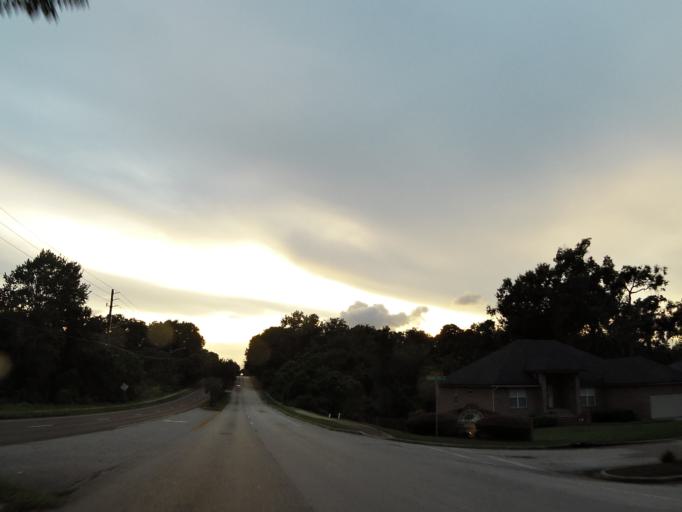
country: US
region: Florida
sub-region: Duval County
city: Jacksonville
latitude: 30.3667
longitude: -81.5789
